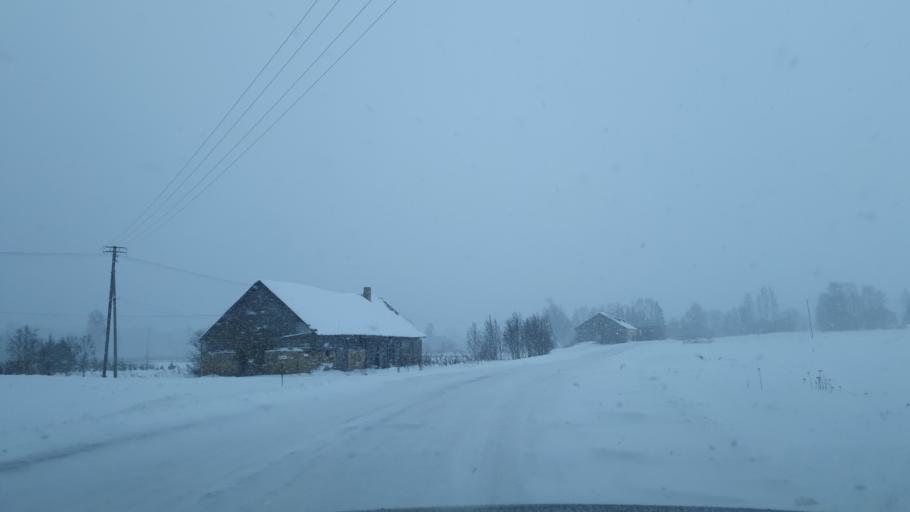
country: EE
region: Jaervamaa
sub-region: Jaerva-Jaani vald
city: Jarva-Jaani
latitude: 59.0521
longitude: 25.8529
